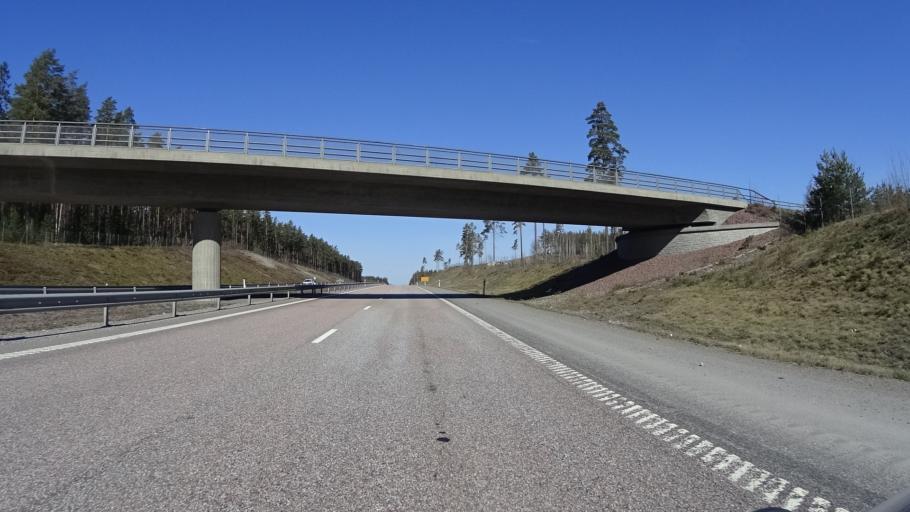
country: SE
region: Soedermanland
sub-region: Strangnas Kommun
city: Akers Styckebruk
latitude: 59.3019
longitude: 17.0841
